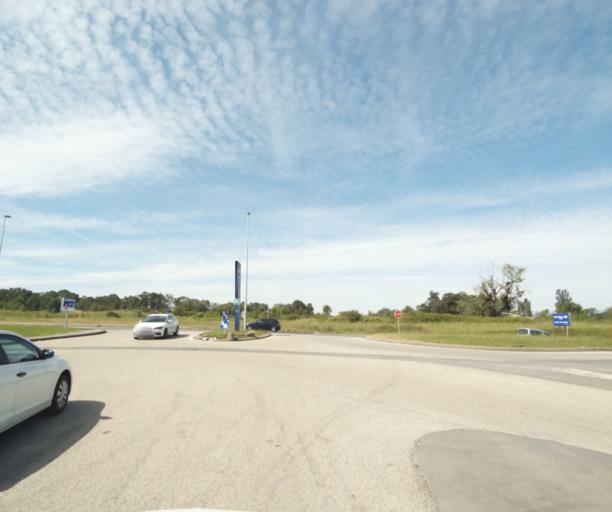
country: FR
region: Rhone-Alpes
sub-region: Departement de la Haute-Savoie
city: Anthy-sur-Leman
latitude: 46.3485
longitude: 6.4327
